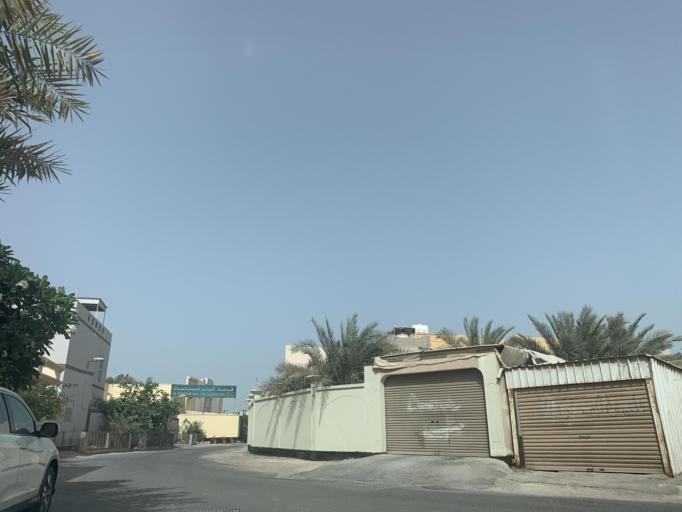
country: BH
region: Northern
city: Sitrah
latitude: 26.1704
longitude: 50.6234
